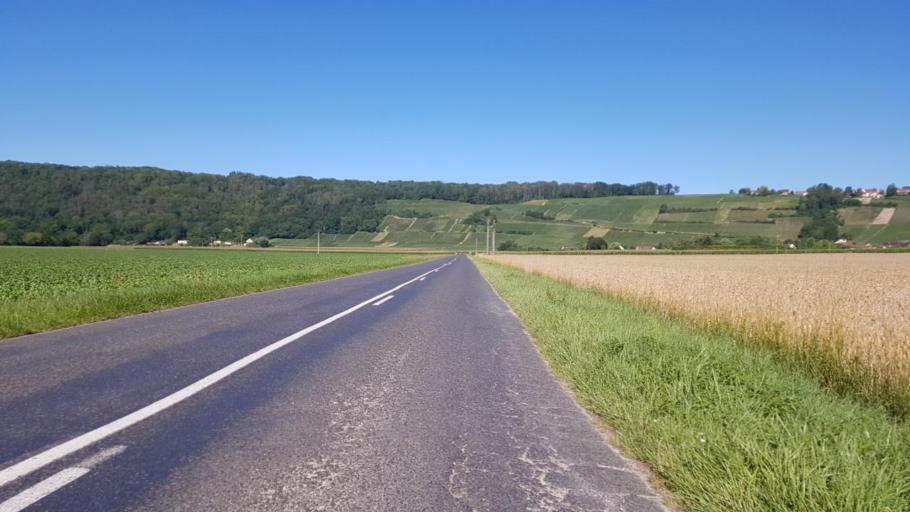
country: FR
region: Picardie
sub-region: Departement de l'Aisne
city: Chezy-sur-Marne
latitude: 49.0025
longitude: 3.3564
